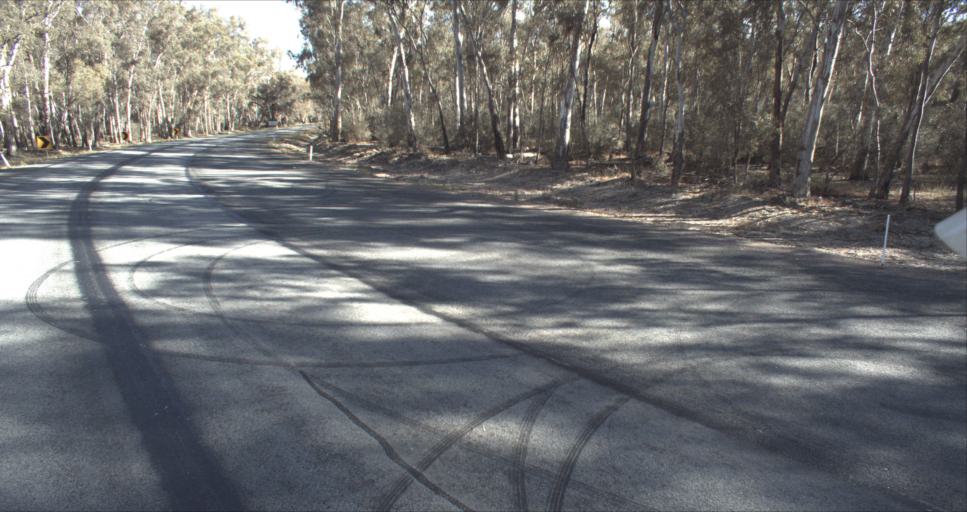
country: AU
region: New South Wales
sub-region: Leeton
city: Leeton
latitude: -34.6332
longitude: 146.3754
